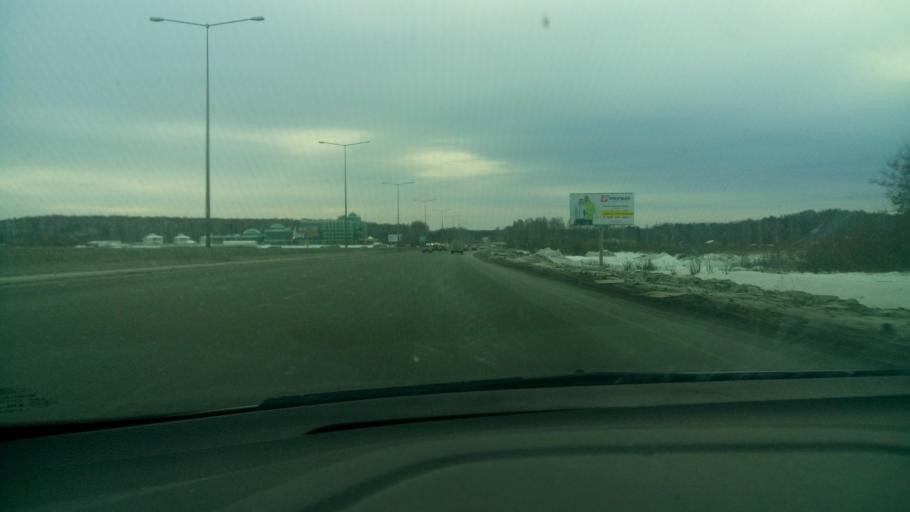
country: RU
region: Sverdlovsk
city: Istok
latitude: 56.7791
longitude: 60.7082
